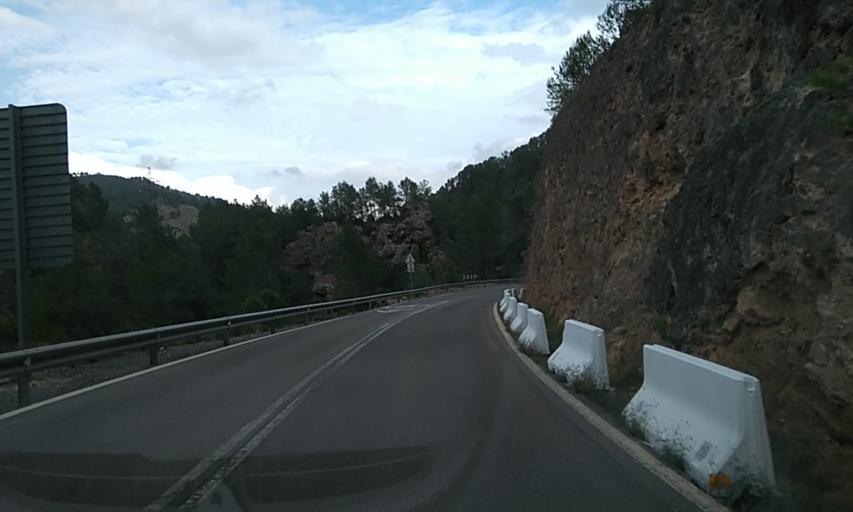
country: ES
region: Valencia
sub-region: Provincia de Castello
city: Montanejos
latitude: 40.0745
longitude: -0.5365
